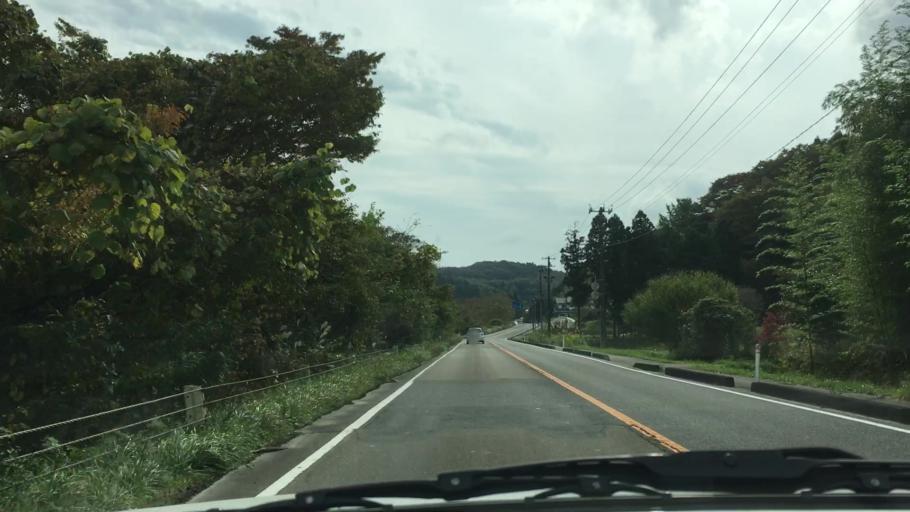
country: JP
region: Miyagi
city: Matsushima
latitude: 38.4251
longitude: 141.0603
